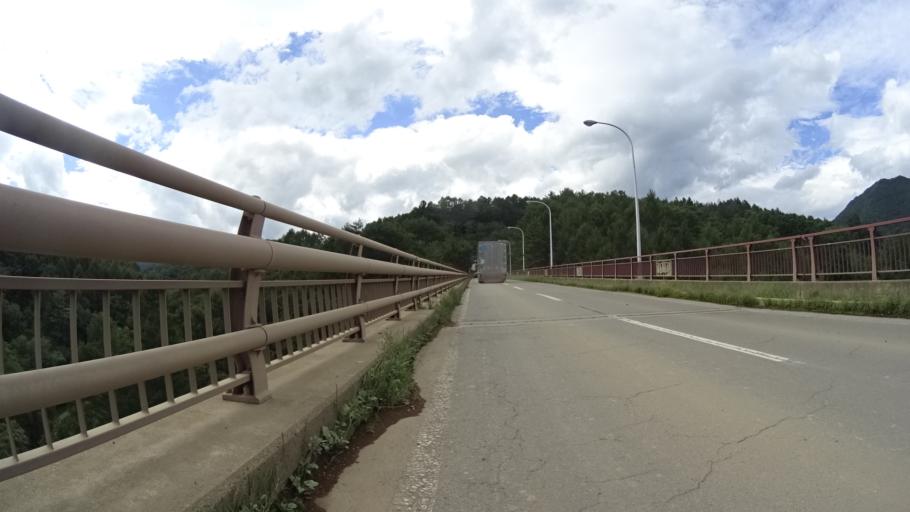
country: JP
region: Nagano
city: Saku
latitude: 35.9631
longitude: 138.5388
